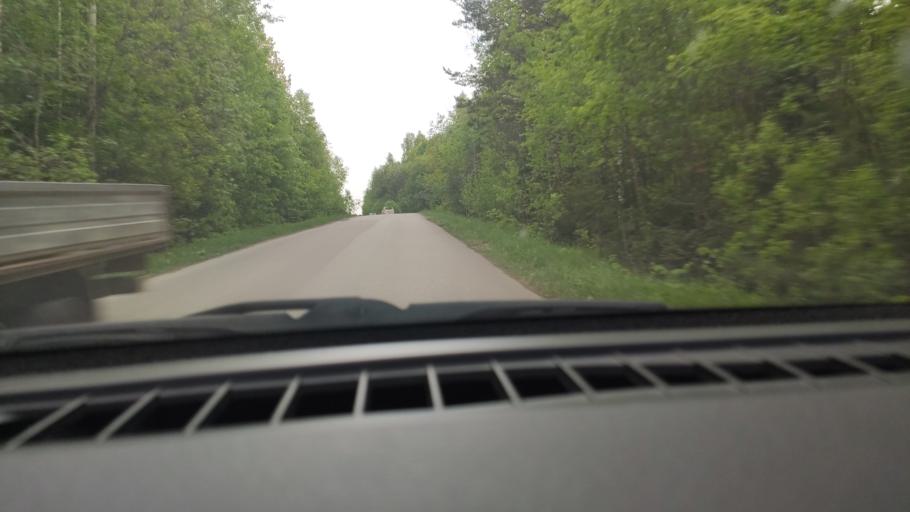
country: RU
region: Perm
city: Overyata
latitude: 58.0677
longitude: 56.0017
